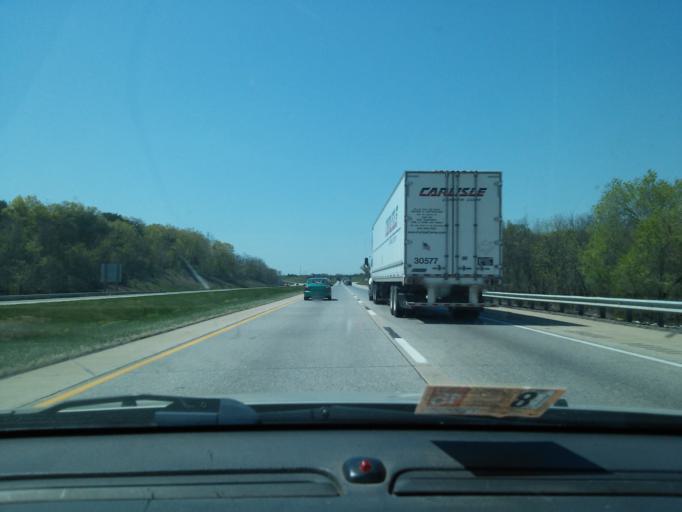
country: US
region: Pennsylvania
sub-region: Dauphin County
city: Skyline View
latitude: 40.3590
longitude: -76.7121
